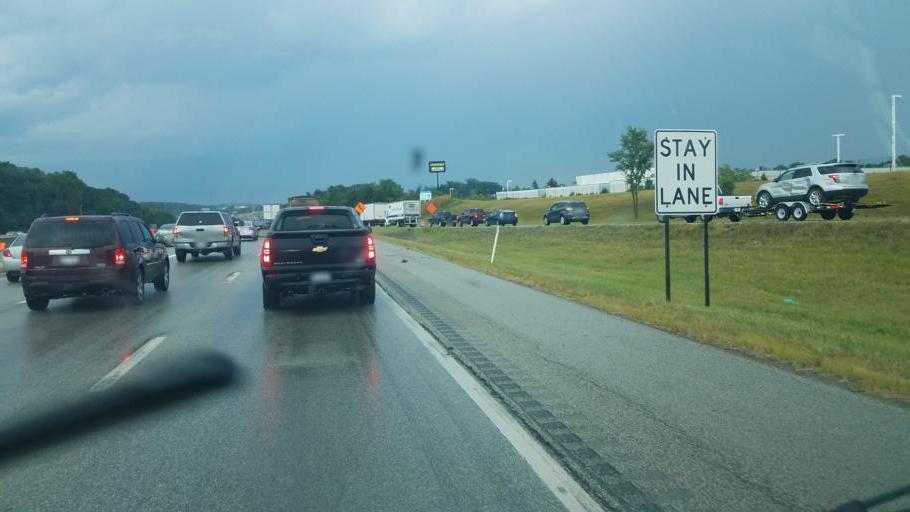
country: US
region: Ohio
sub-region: Cuyahoga County
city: Oakwood
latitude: 41.3748
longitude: -81.5135
